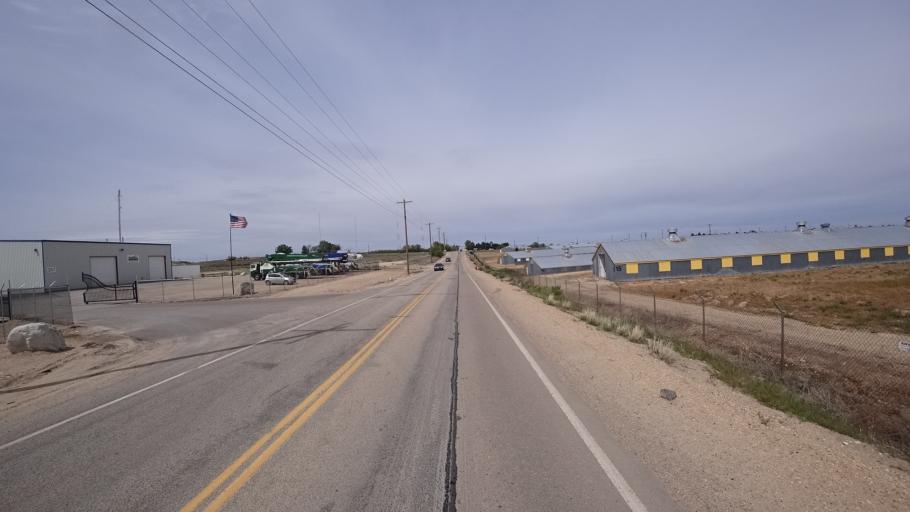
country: US
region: Idaho
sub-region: Ada County
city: Meridian
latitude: 43.5611
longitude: -116.3892
